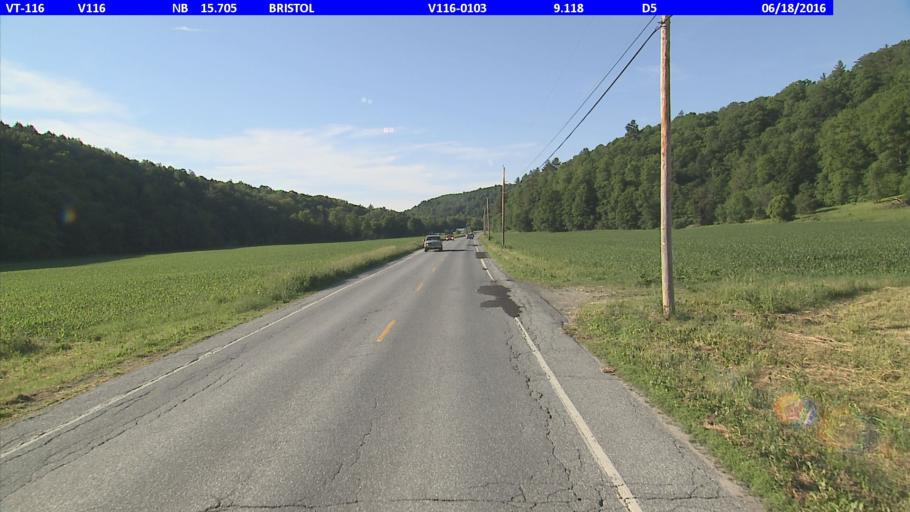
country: US
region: Vermont
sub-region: Addison County
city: Bristol
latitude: 44.1422
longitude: -73.0455
